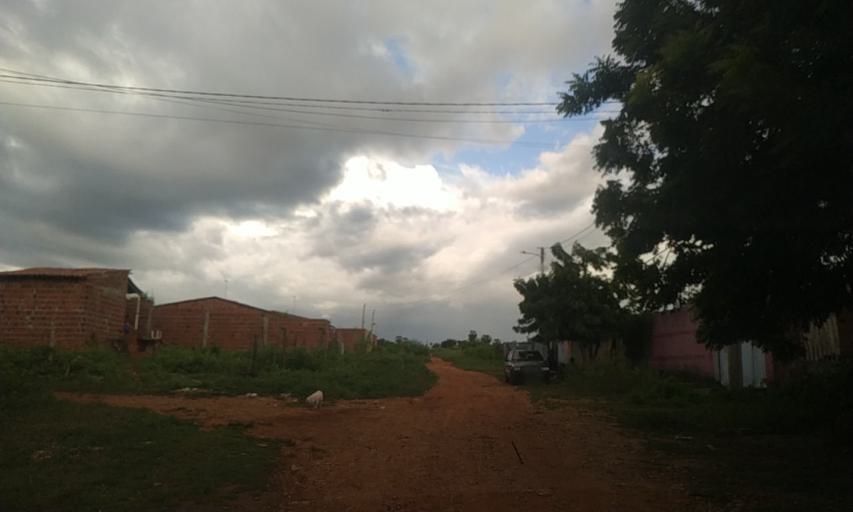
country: BR
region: Rio Grande do Norte
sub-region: Mossoro
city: Mossoro
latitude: -5.2186
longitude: -37.3470
